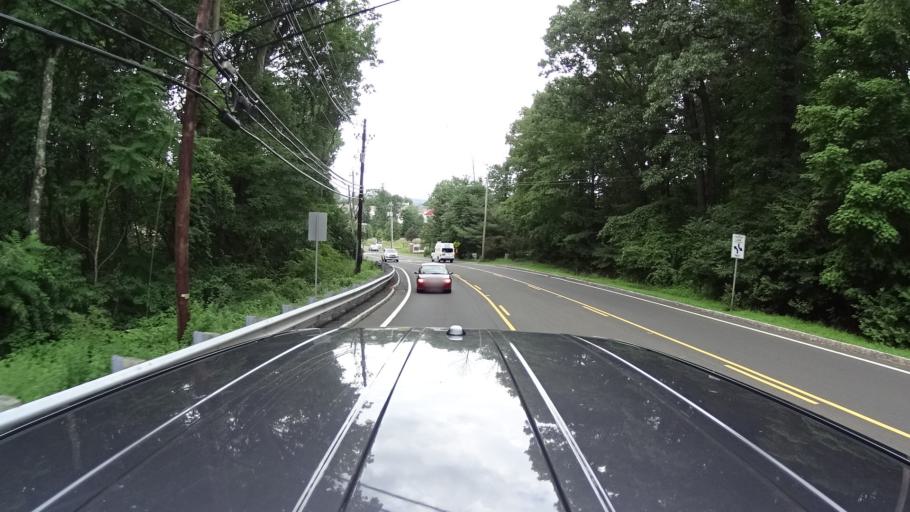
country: US
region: New Jersey
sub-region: Somerset County
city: Warren Township
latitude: 40.6405
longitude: -74.5148
